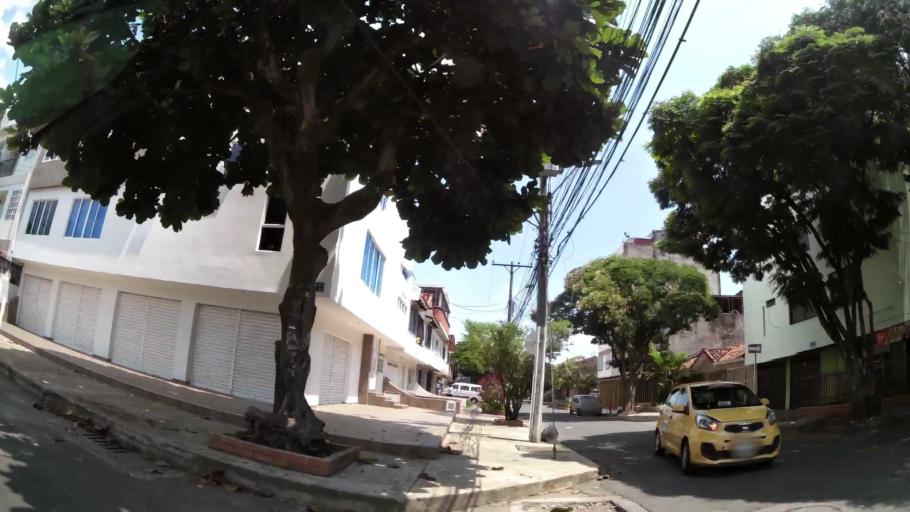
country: CO
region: Valle del Cauca
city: Cali
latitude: 3.4019
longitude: -76.5405
